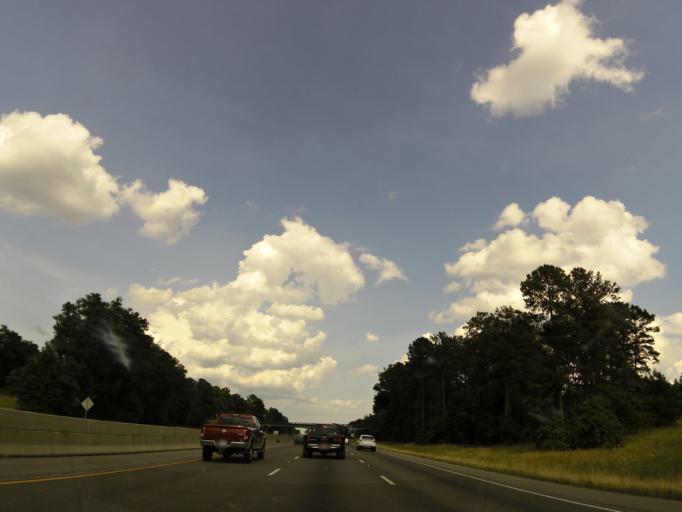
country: US
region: Alabama
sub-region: Tuscaloosa County
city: Coaling
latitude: 33.1890
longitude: -87.3042
